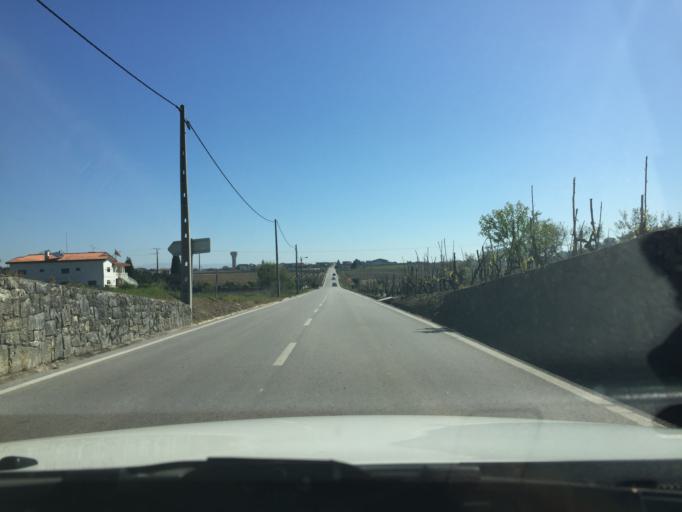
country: PT
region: Coimbra
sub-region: Cantanhede
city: Cantanhede
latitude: 40.4206
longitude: -8.5418
